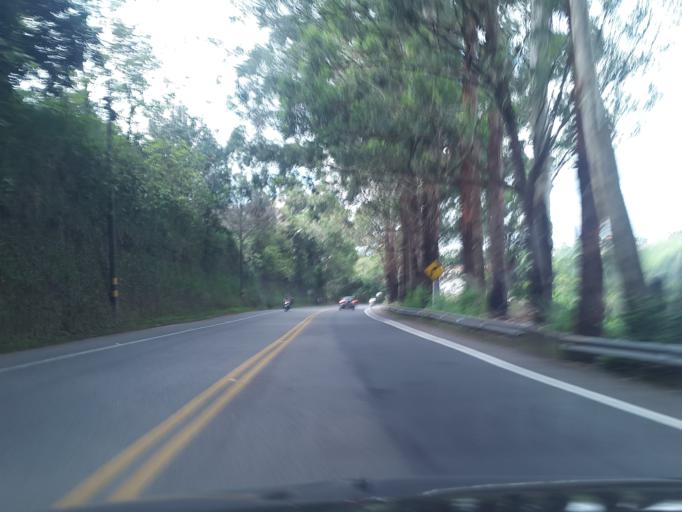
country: CO
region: Quindio
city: Calarca
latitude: 4.5393
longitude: -75.6518
